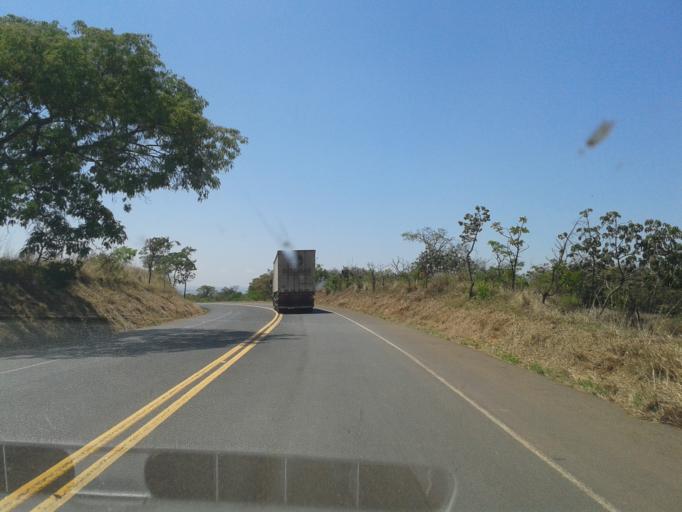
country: BR
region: Minas Gerais
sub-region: Araxa
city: Araxa
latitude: -19.4236
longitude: -47.2535
